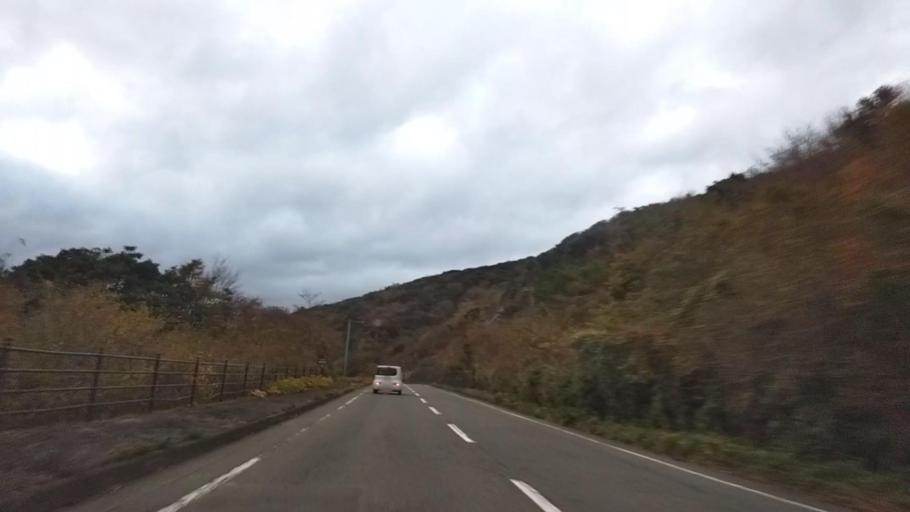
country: JP
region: Kanagawa
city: Hakone
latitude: 35.1693
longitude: 139.0258
